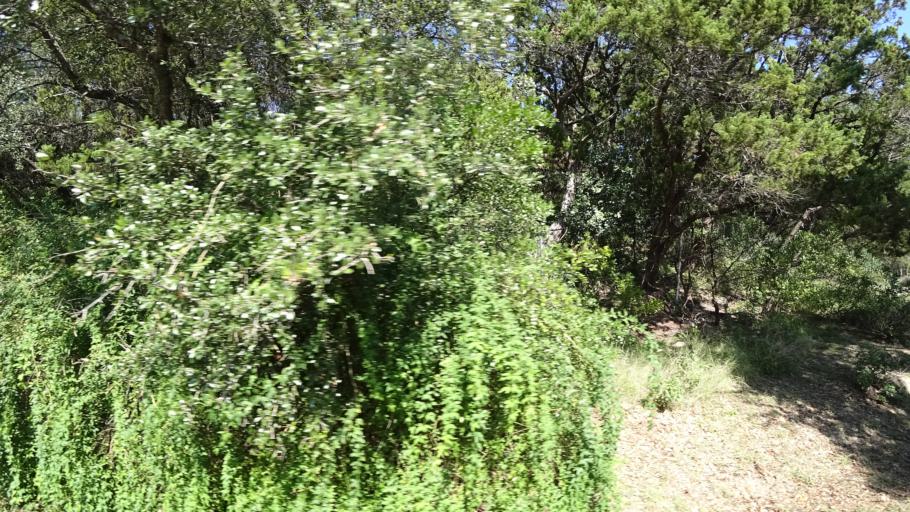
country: US
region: Texas
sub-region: Travis County
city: West Lake Hills
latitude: 30.2959
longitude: -97.7995
